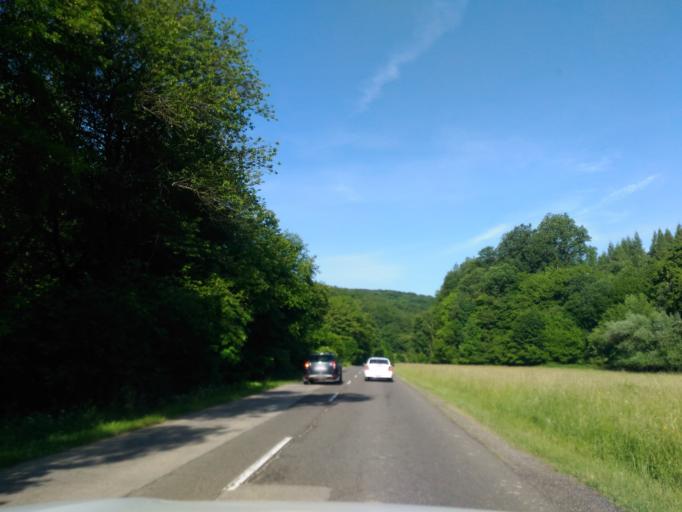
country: HU
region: Baranya
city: Komlo
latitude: 46.1952
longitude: 18.3120
